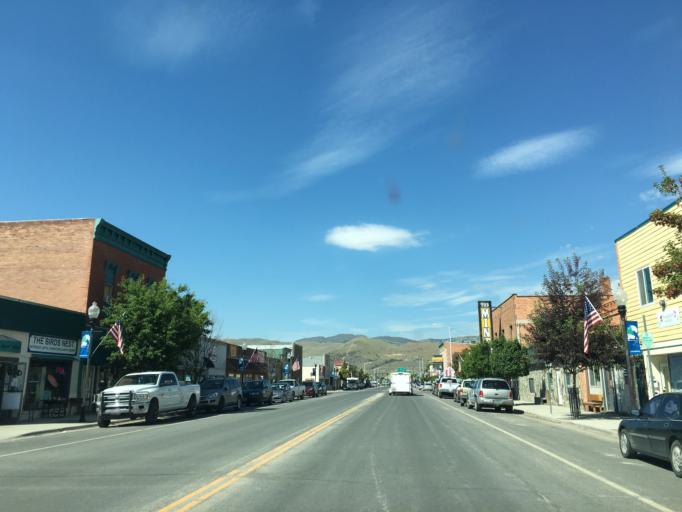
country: US
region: Montana
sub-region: Broadwater County
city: Townsend
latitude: 46.3204
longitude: -111.5176
